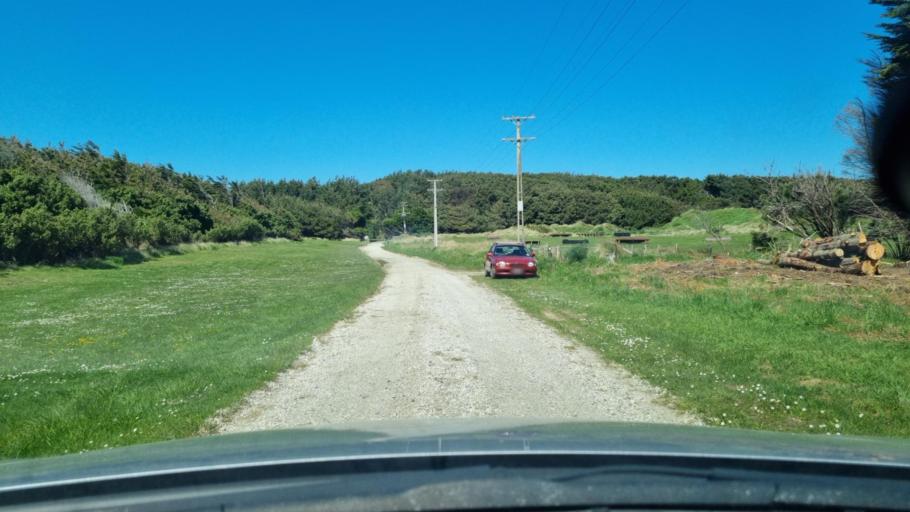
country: NZ
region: Southland
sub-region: Invercargill City
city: Invercargill
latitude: -46.4394
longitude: 168.2394
